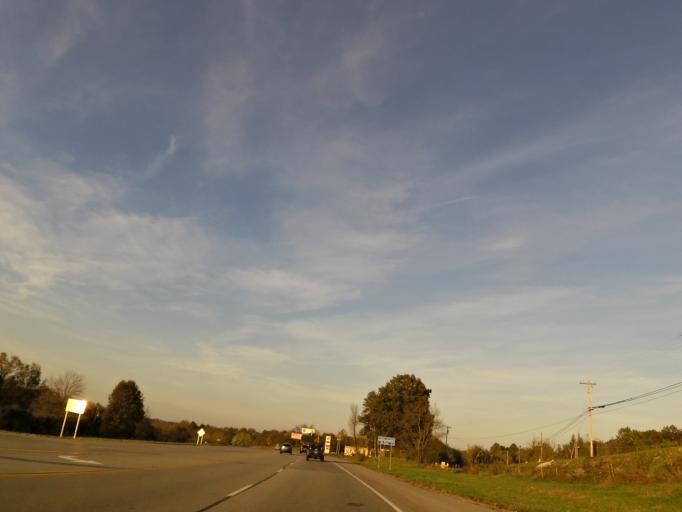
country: US
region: Kentucky
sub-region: Jessamine County
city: Wilmore
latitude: 37.7512
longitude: -84.6189
